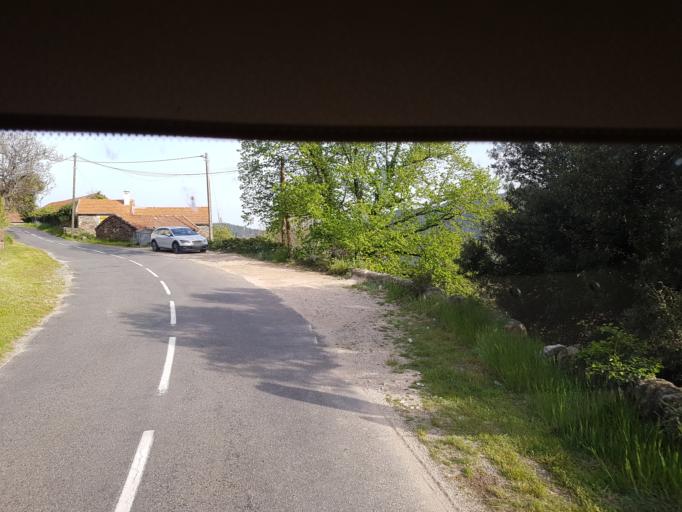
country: FR
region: Languedoc-Roussillon
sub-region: Departement du Gard
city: Branoux-les-Taillades
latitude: 44.3315
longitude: 3.9236
